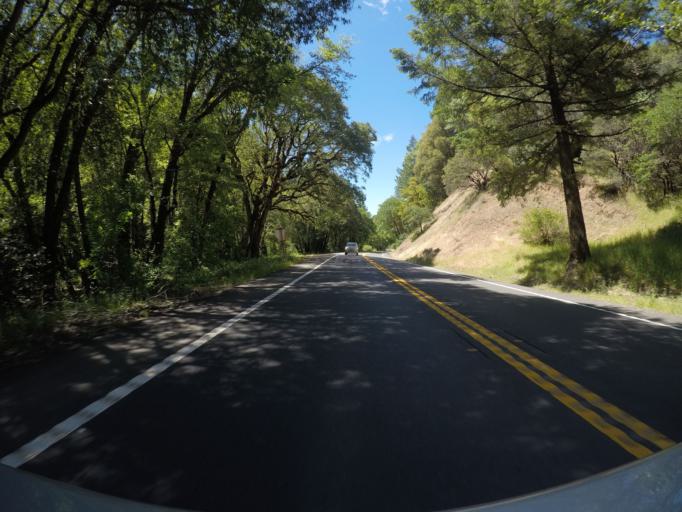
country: US
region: California
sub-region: Mendocino County
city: Laytonville
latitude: 39.8133
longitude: -123.5585
